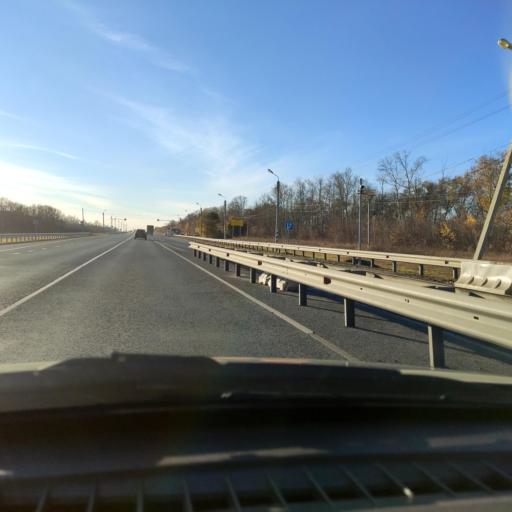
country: RU
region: Samara
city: Varlamovo
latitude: 53.1952
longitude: 48.2644
